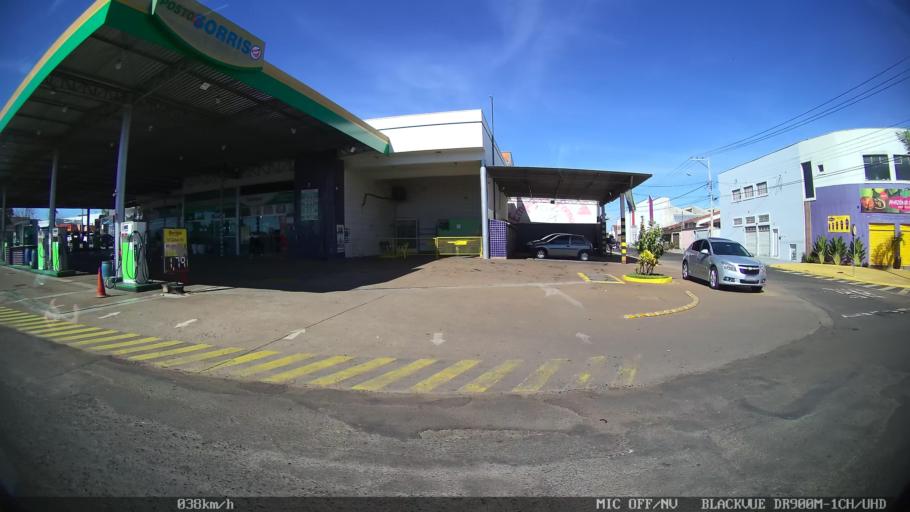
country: BR
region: Sao Paulo
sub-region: Franca
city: Franca
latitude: -20.5425
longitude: -47.3764
